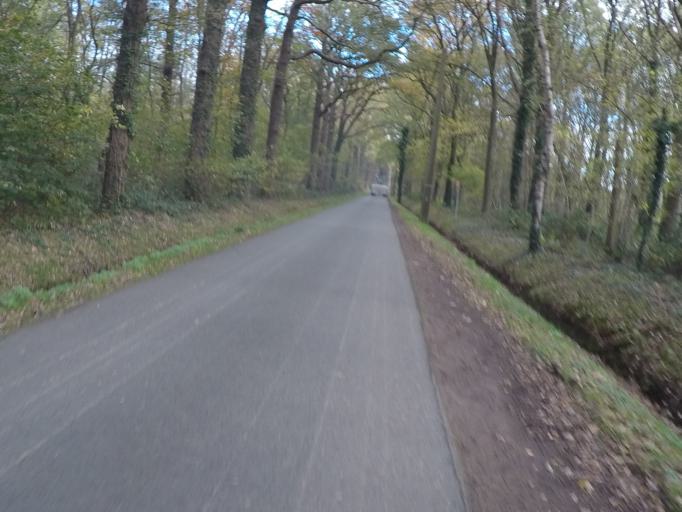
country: BE
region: Flanders
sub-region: Provincie Antwerpen
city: Berlaar
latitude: 51.1298
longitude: 4.6411
